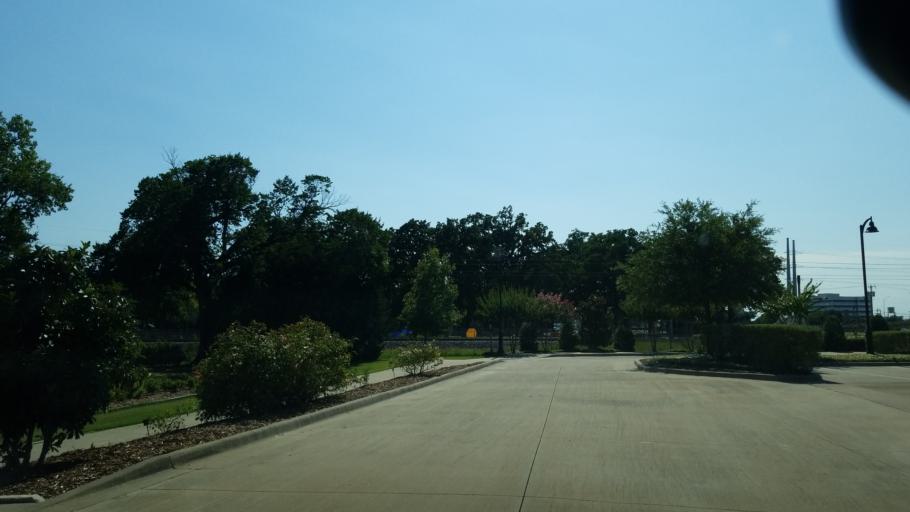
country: US
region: Texas
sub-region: Dallas County
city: Farmers Branch
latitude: 32.9202
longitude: -96.8951
